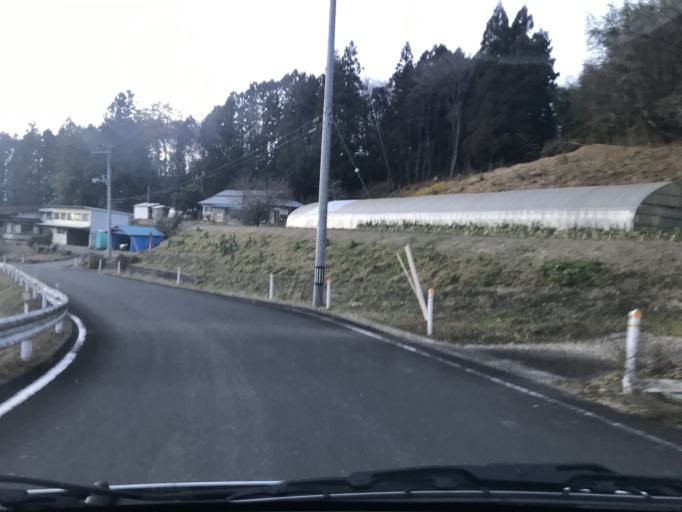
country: JP
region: Iwate
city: Ichinoseki
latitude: 38.8295
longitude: 141.0882
